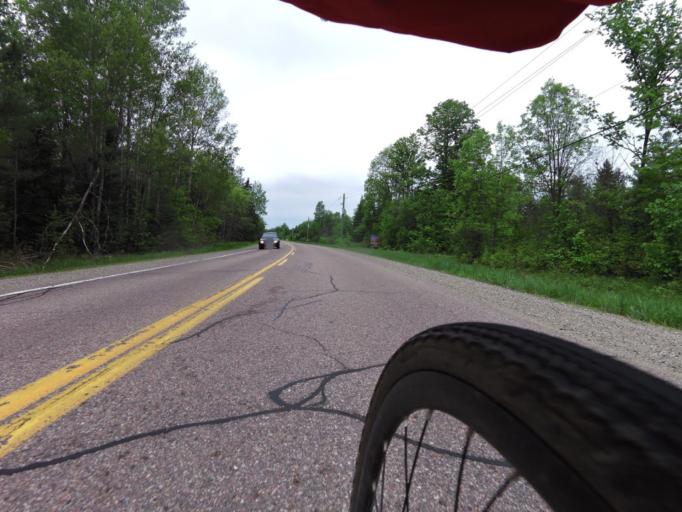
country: CA
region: Ontario
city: Renfrew
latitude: 45.2899
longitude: -76.6892
